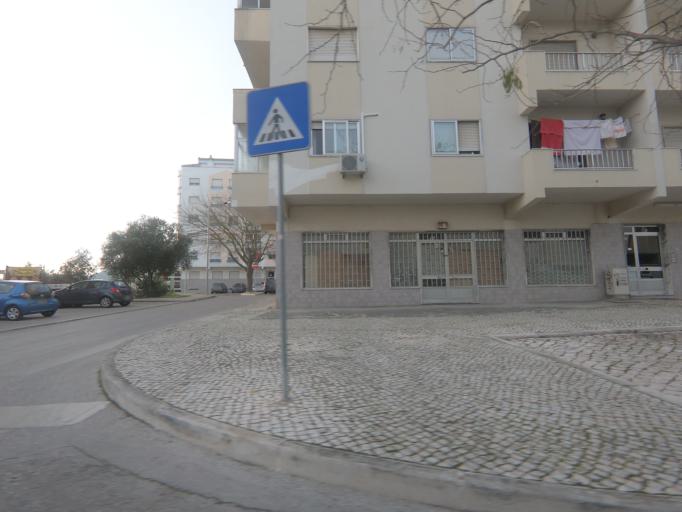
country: PT
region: Setubal
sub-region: Setubal
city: Setubal
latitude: 38.5325
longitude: -8.8766
